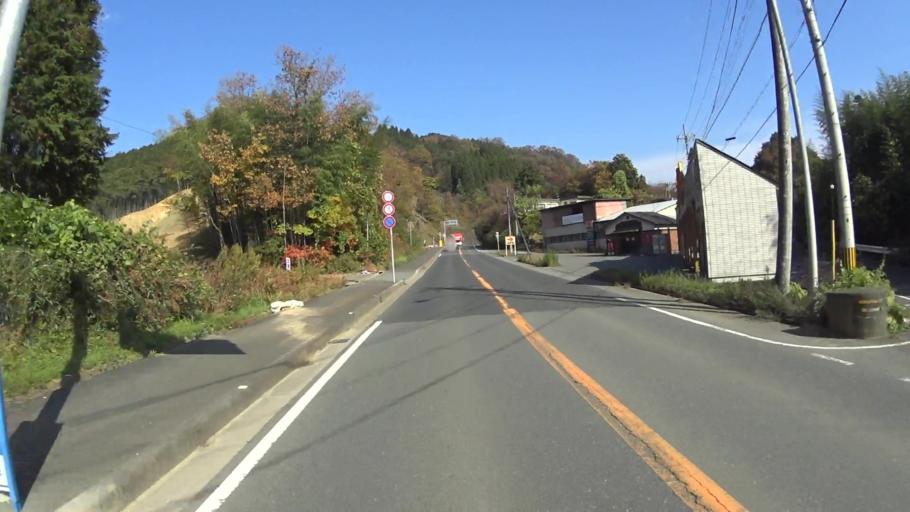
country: JP
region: Kyoto
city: Miyazu
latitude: 35.4194
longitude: 135.2039
